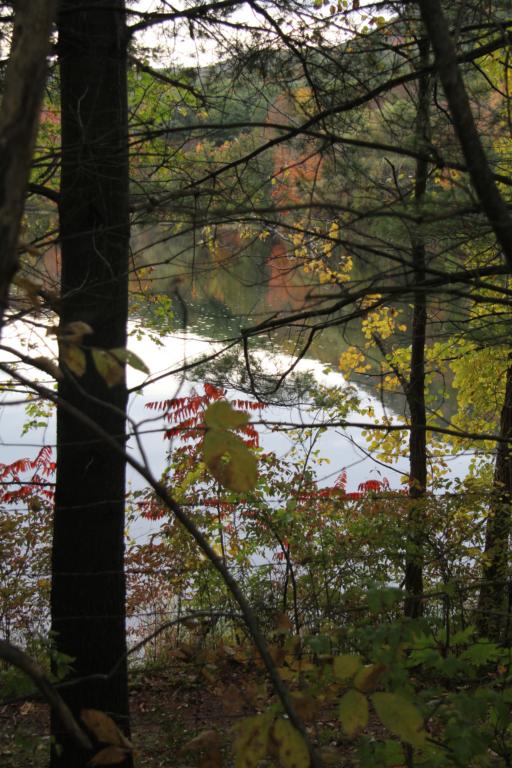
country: US
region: Connecticut
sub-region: Litchfield County
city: Canaan
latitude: 42.0371
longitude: -73.4253
